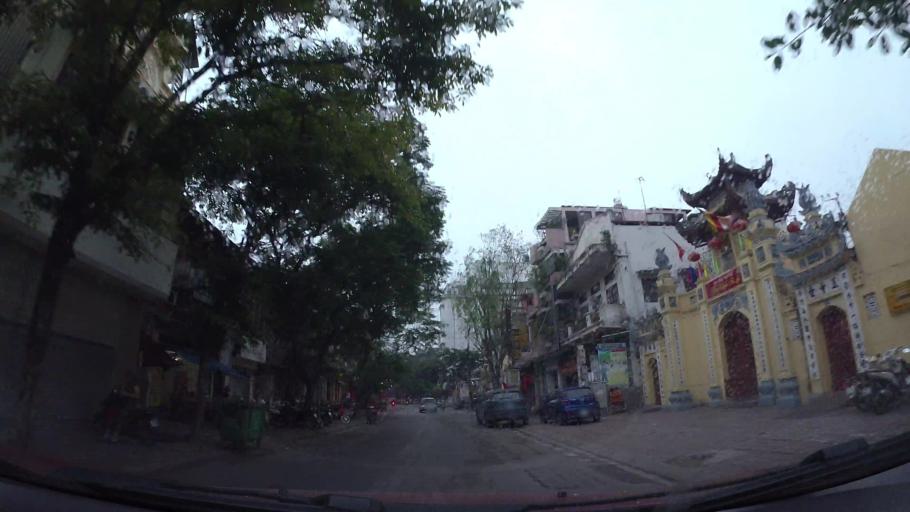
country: VN
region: Ha Noi
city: Hanoi
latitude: 21.0286
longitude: 105.8375
